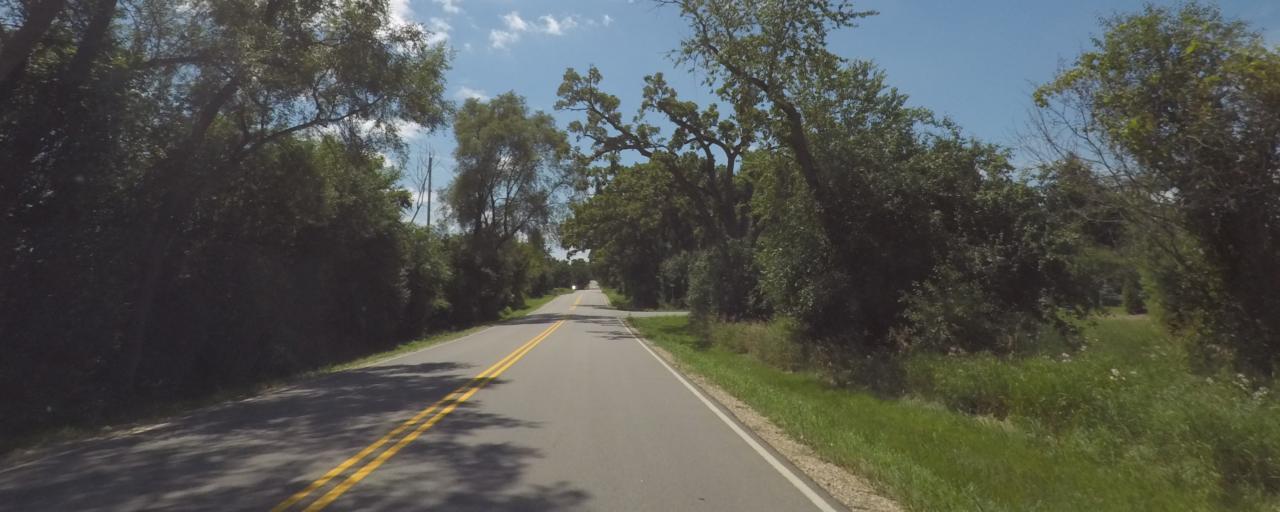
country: US
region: Wisconsin
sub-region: Waukesha County
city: Dousman
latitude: 42.9687
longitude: -88.4592
